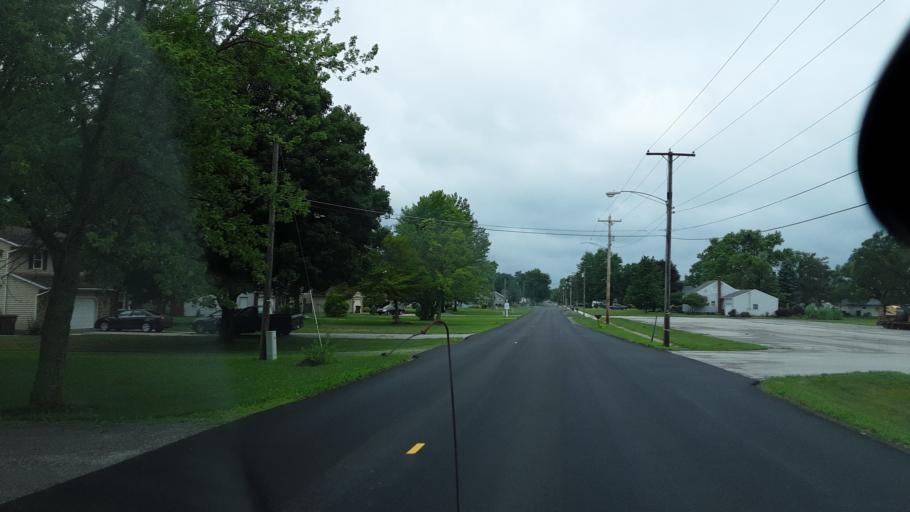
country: US
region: Indiana
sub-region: Allen County
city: Monroeville
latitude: 40.9483
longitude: -84.9820
